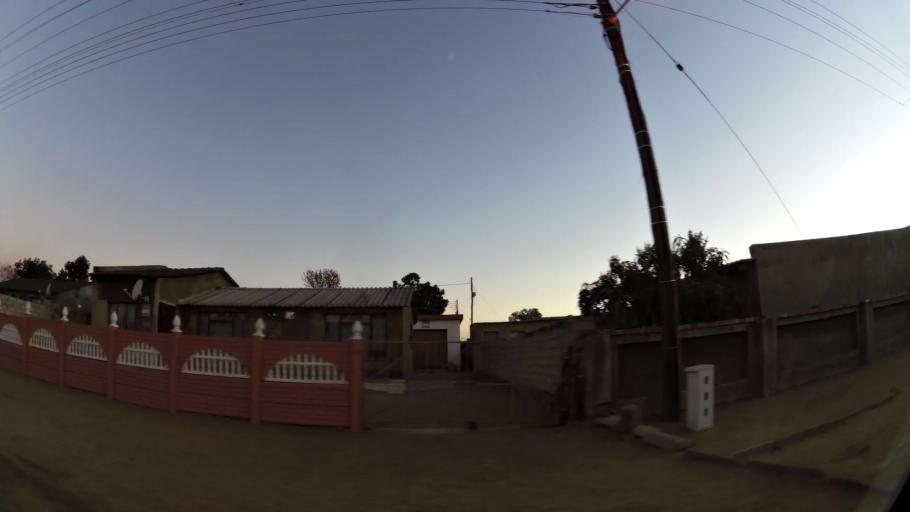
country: ZA
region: Limpopo
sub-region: Capricorn District Municipality
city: Polokwane
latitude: -23.8579
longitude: 29.3871
